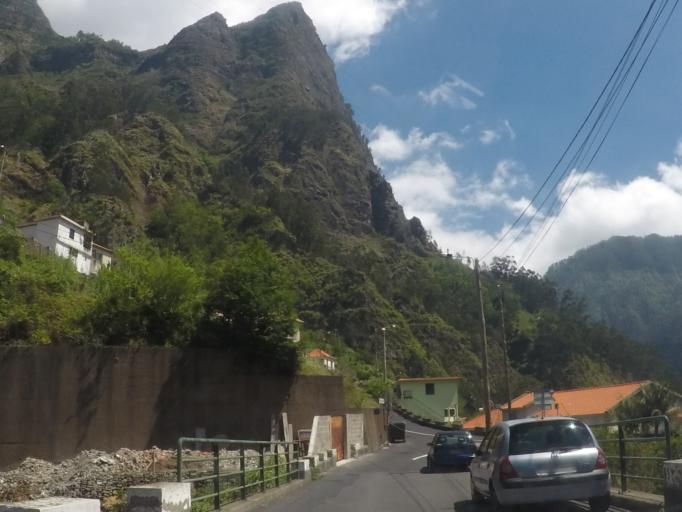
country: PT
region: Madeira
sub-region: Camara de Lobos
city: Curral das Freiras
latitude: 32.7166
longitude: -16.9683
